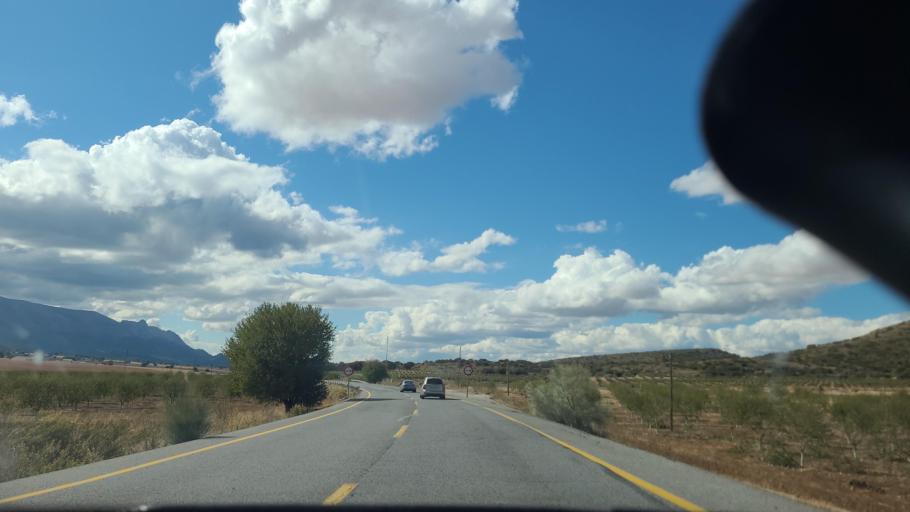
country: ES
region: Andalusia
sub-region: Provincia de Granada
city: Pinar
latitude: 37.4057
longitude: -3.3907
